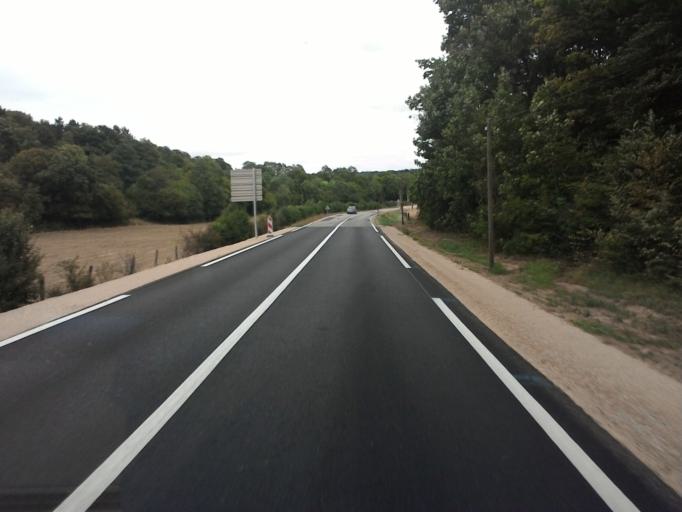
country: FR
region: Lorraine
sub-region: Departement de Meurthe-et-Moselle
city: Colombey-les-Belles
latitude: 48.5726
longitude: 5.9625
